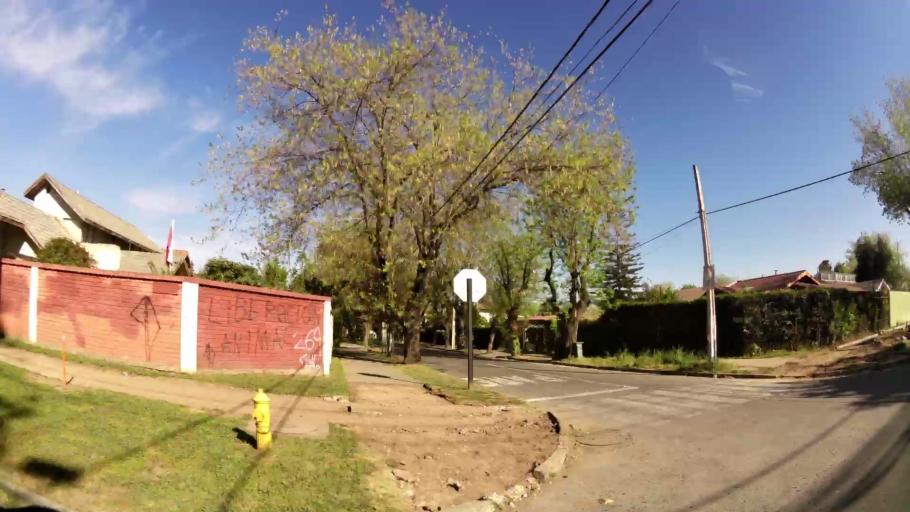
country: CL
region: Santiago Metropolitan
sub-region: Provincia de Santiago
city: Villa Presidente Frei, Nunoa, Santiago, Chile
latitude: -33.4326
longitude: -70.5547
